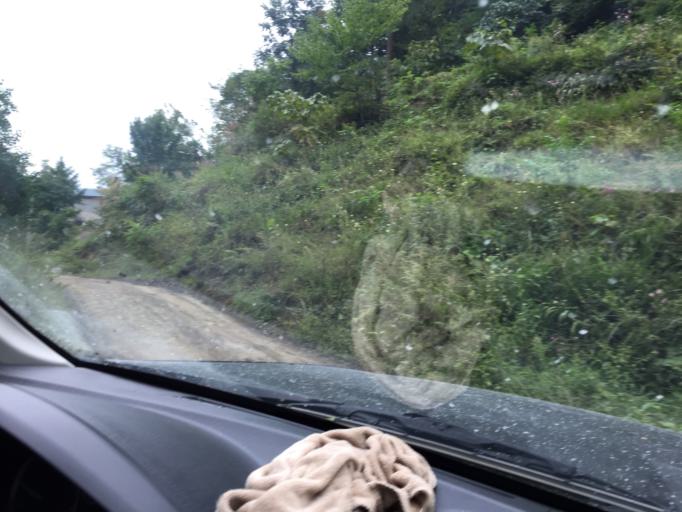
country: CN
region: Guizhou Sheng
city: Nangan
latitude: 28.2535
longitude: 107.9465
